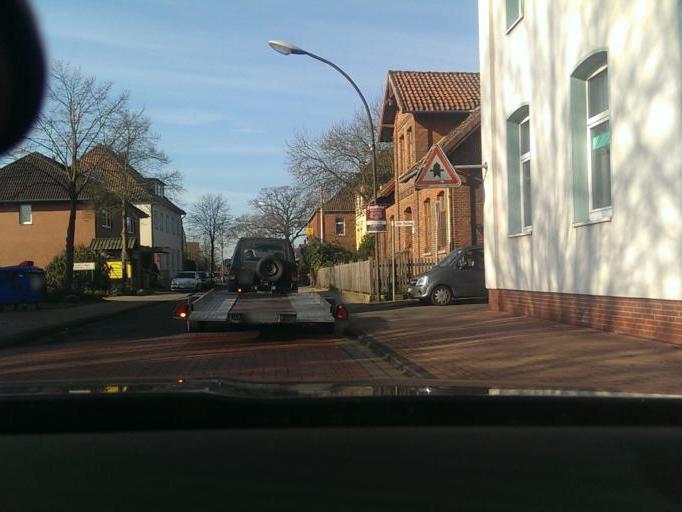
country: DE
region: Lower Saxony
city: Schwarmstedt
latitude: 52.6785
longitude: 9.6236
